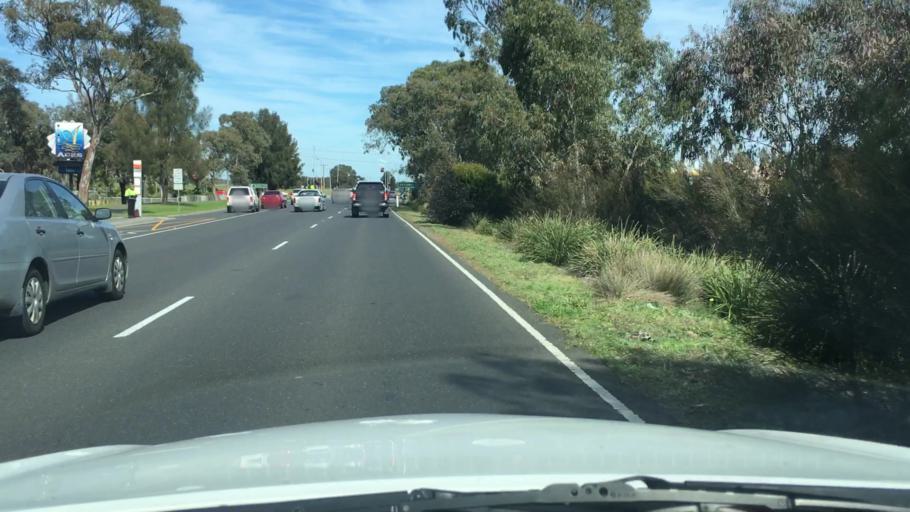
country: AU
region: Victoria
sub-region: Kingston
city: Waterways
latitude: -38.0088
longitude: 145.1412
